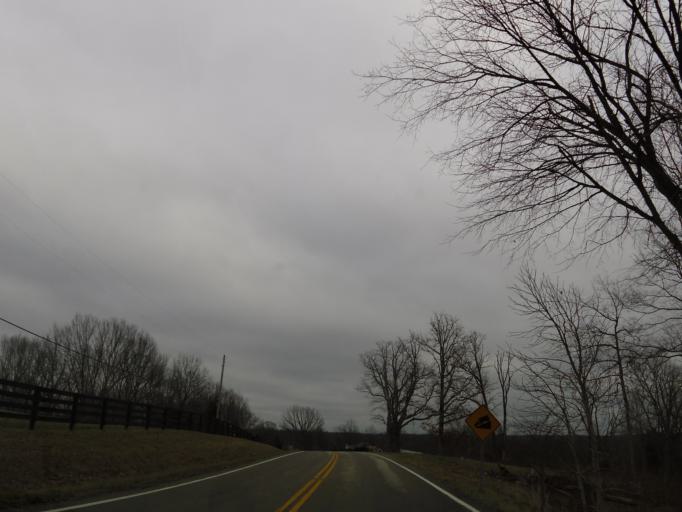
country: US
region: Kentucky
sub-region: Henry County
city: Eminence
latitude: 38.3463
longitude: -85.0102
